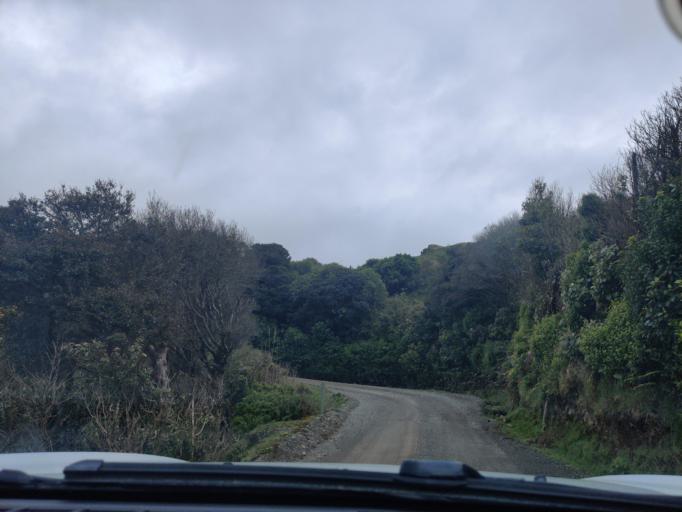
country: NZ
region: Manawatu-Wanganui
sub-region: Palmerston North City
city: Palmerston North
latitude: -40.2750
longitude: 175.8518
